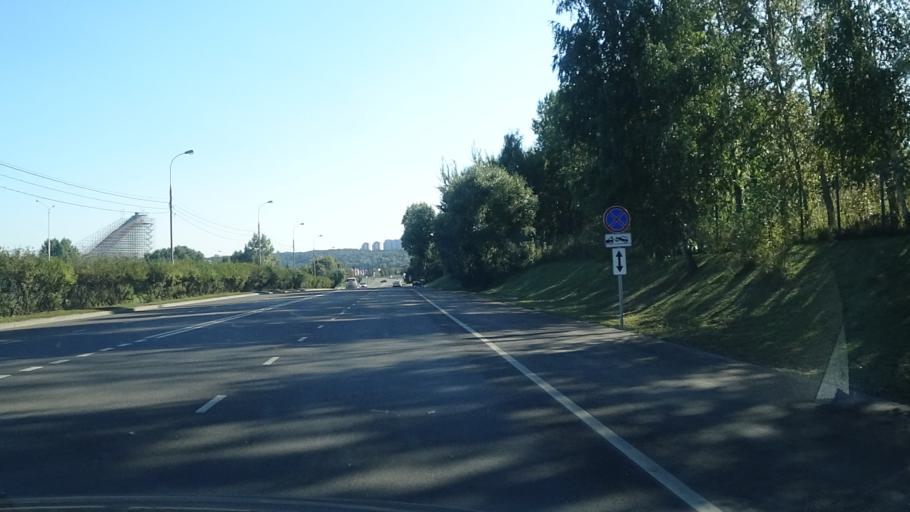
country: RU
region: Moscow
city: Shchukino
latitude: 55.7602
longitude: 37.4312
